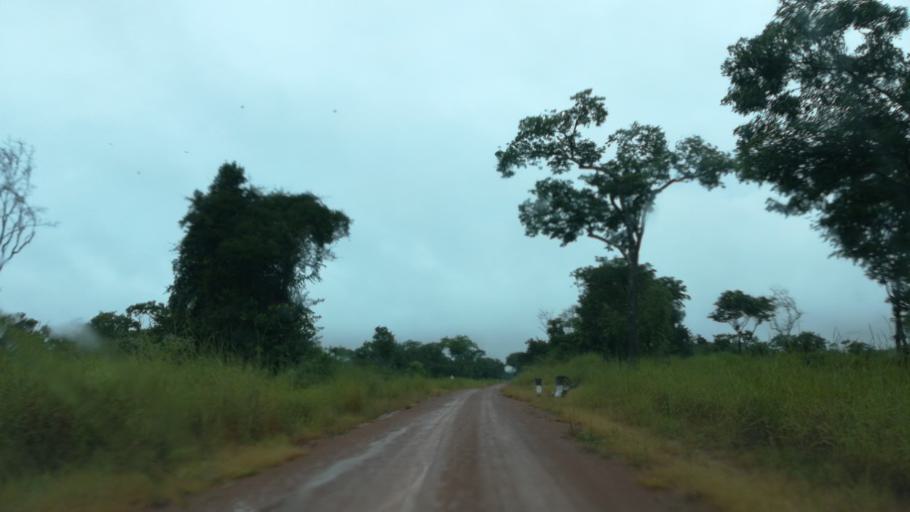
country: ZM
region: Luapula
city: Mwense
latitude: -10.7074
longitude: 28.1765
